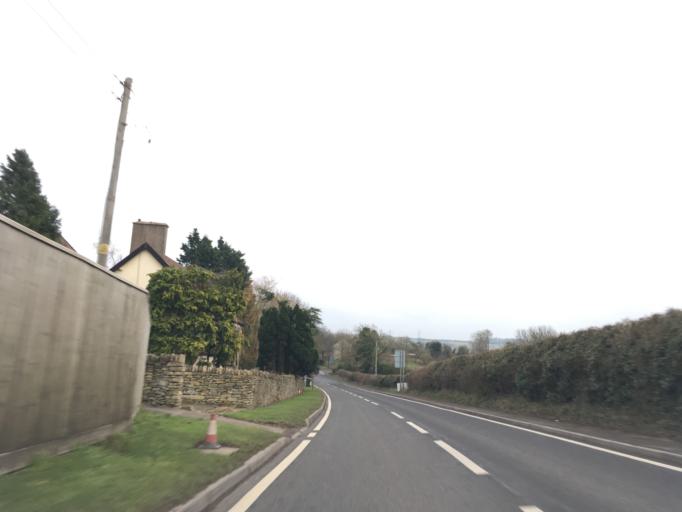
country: GB
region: England
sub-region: South Gloucestershire
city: Hinton
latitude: 51.5099
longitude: -2.3985
